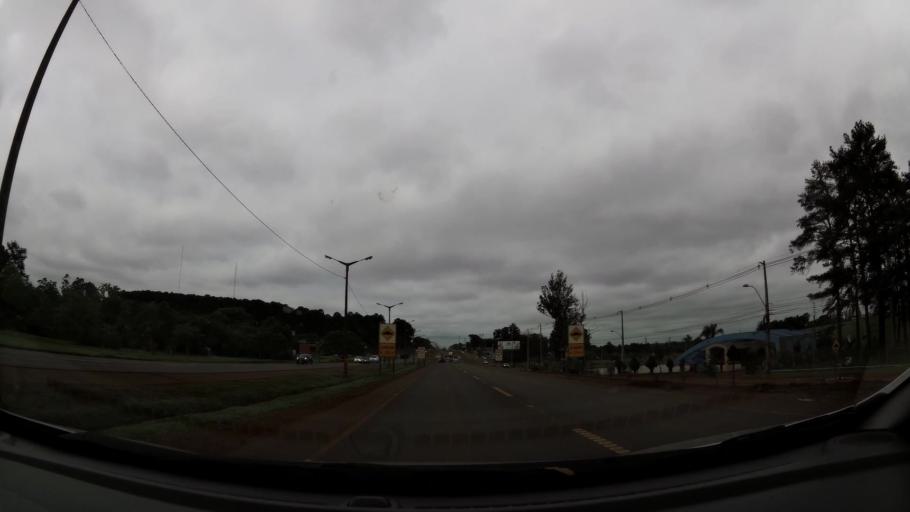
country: PY
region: Alto Parana
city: Ciudad del Este
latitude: -25.4948
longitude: -54.7024
